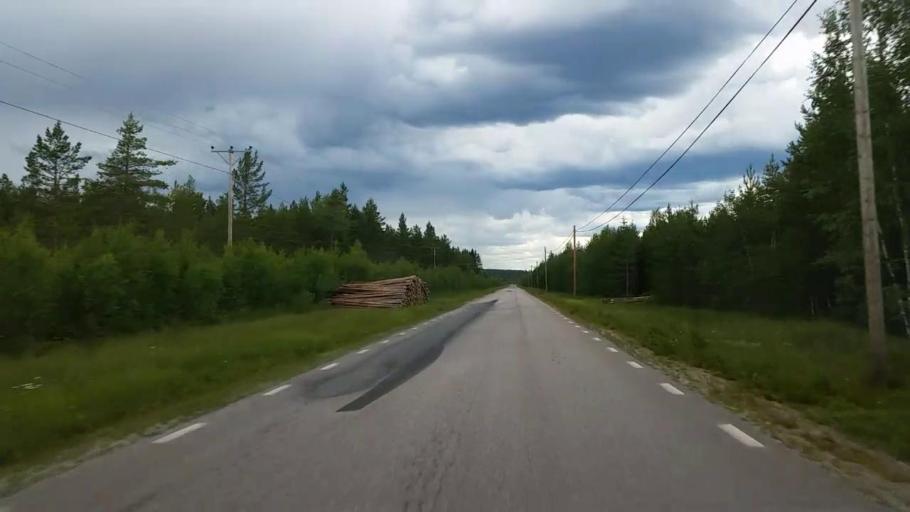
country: SE
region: Gaevleborg
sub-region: Ovanakers Kommun
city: Edsbyn
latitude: 61.4411
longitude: 15.8901
